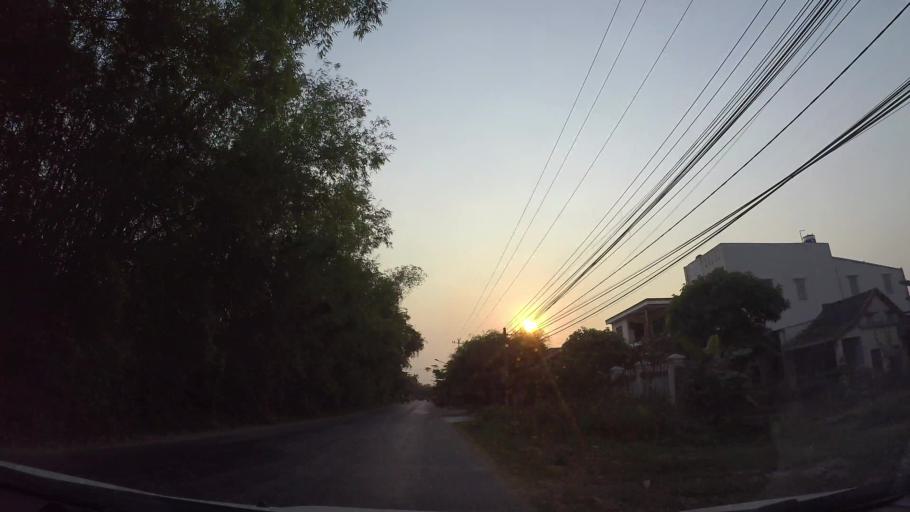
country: VN
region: Quang Nam
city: Quang Nam
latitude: 15.9518
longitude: 108.2326
